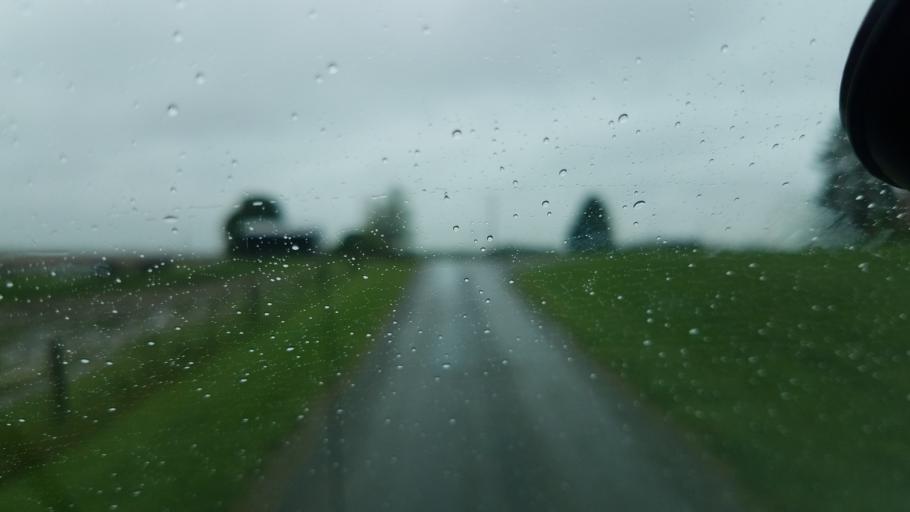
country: US
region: Ohio
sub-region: Highland County
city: Greenfield
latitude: 39.3306
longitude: -83.4433
